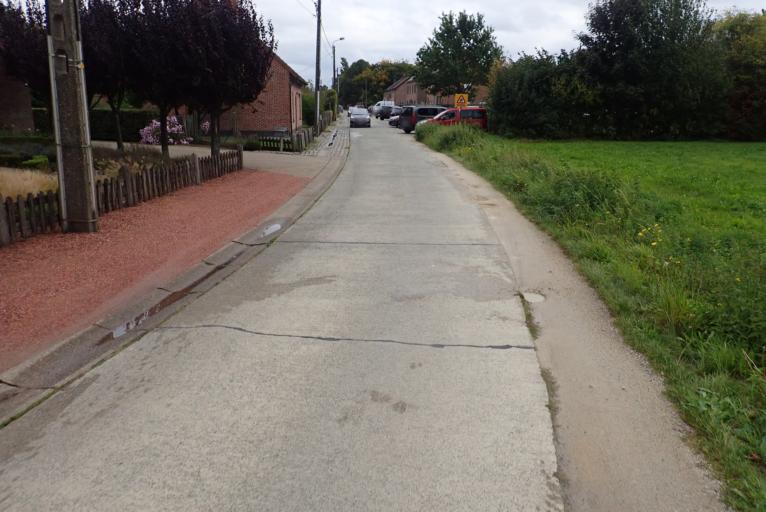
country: BE
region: Flanders
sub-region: Provincie Antwerpen
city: Berlaar
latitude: 51.0858
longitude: 4.6639
